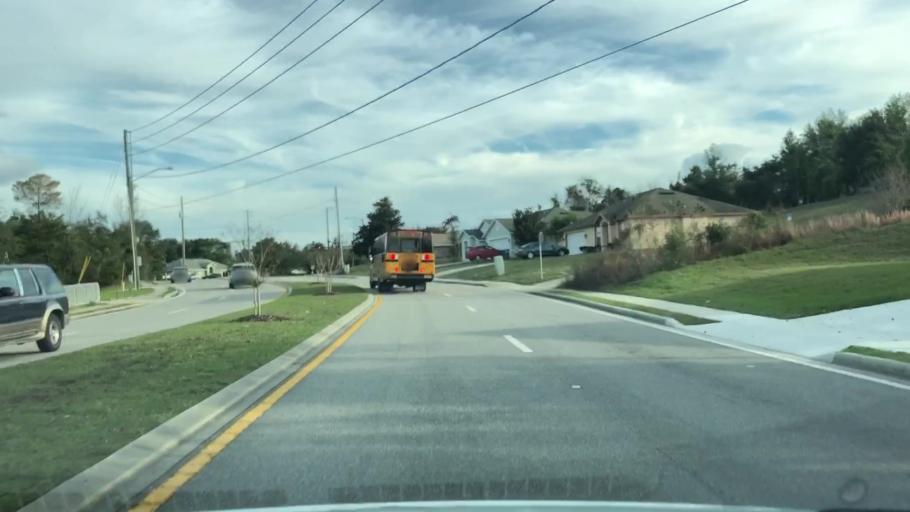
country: US
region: Florida
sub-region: Volusia County
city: Deltona
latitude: 28.9249
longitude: -81.2589
